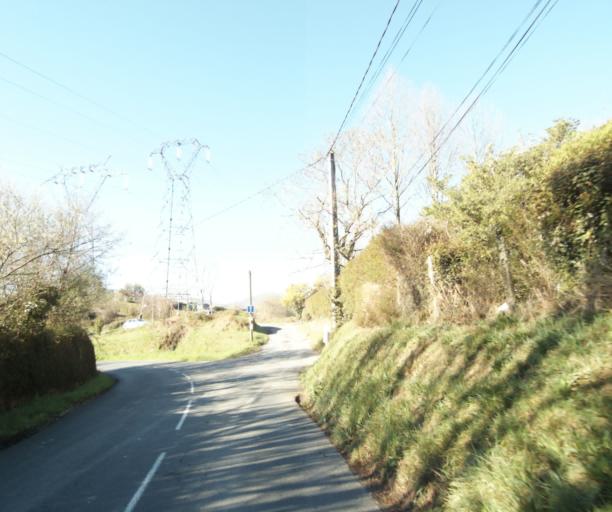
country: FR
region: Aquitaine
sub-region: Departement des Pyrenees-Atlantiques
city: Ciboure
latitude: 43.3513
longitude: -1.6683
